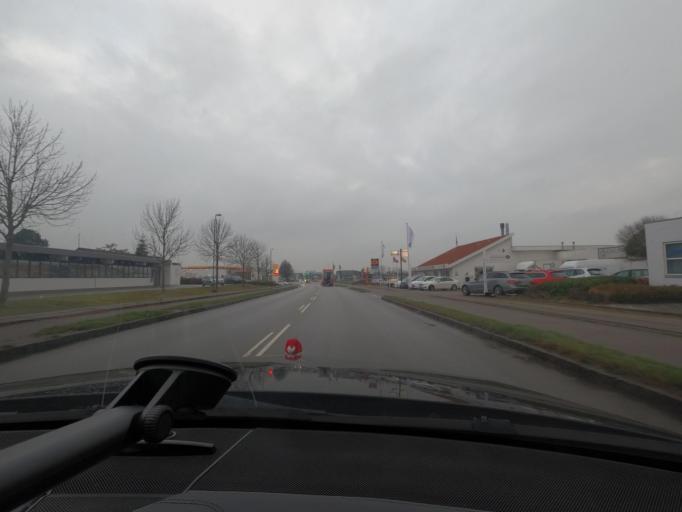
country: DK
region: South Denmark
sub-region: Sonderborg Kommune
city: Sonderborg
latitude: 54.9182
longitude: 9.8103
